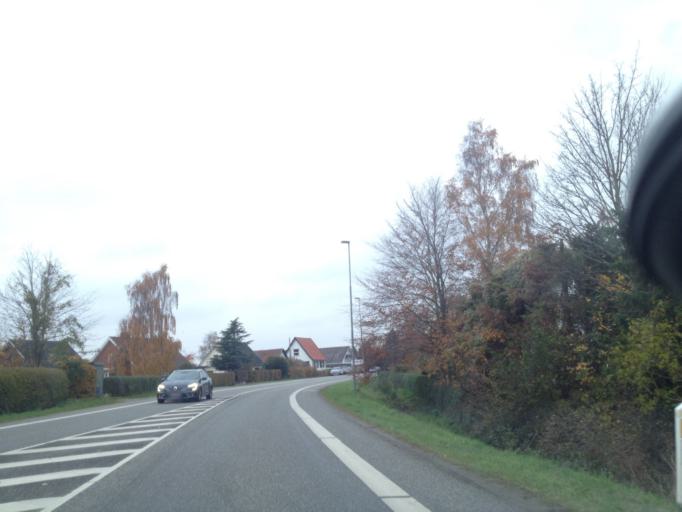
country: DK
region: South Denmark
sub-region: Nordfyns Kommune
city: Sonderso
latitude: 55.4224
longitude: 10.2563
